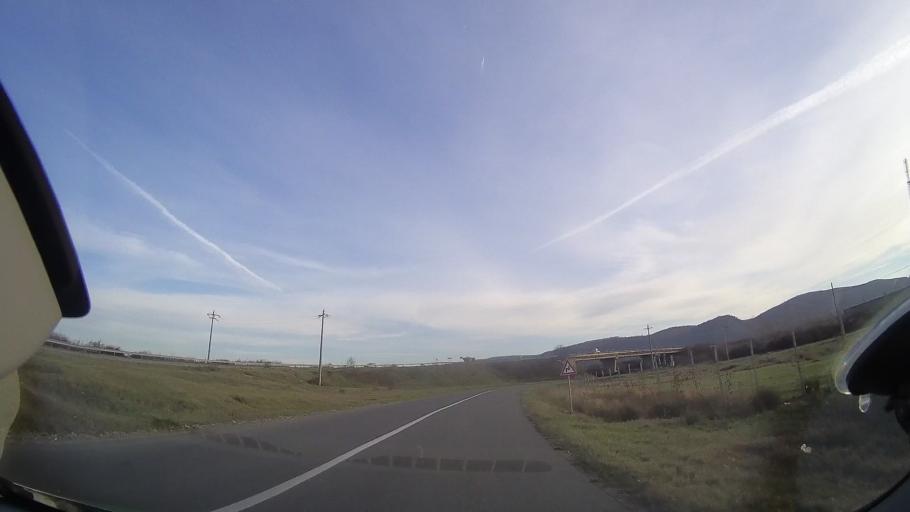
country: RO
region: Bihor
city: Lugasu de Jos
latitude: 47.0423
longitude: 22.3443
